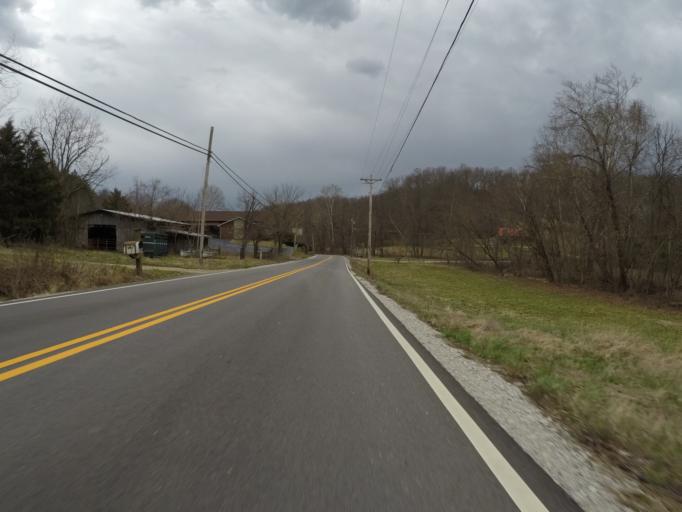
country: US
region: Ohio
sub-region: Lawrence County
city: Burlington
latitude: 38.4439
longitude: -82.5023
